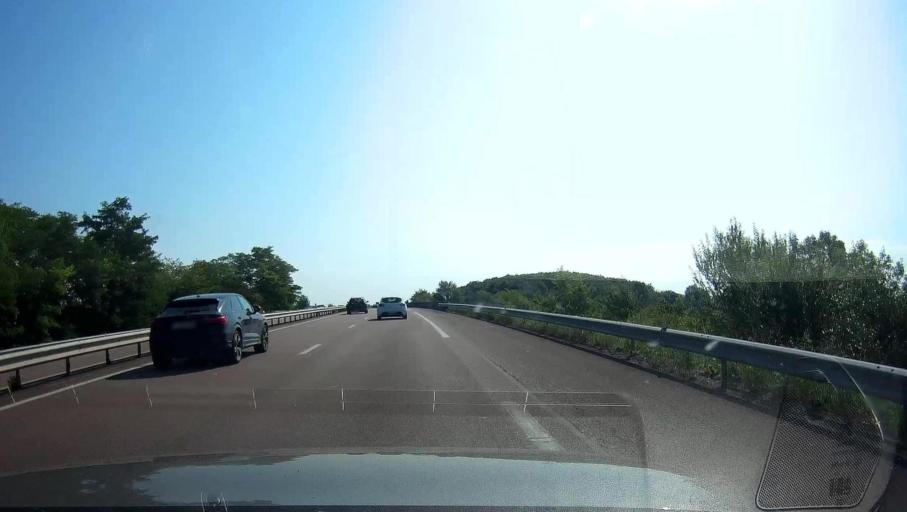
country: FR
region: Bourgogne
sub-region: Departement de la Cote-d'Or
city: Ouges
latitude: 47.2429
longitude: 5.0831
